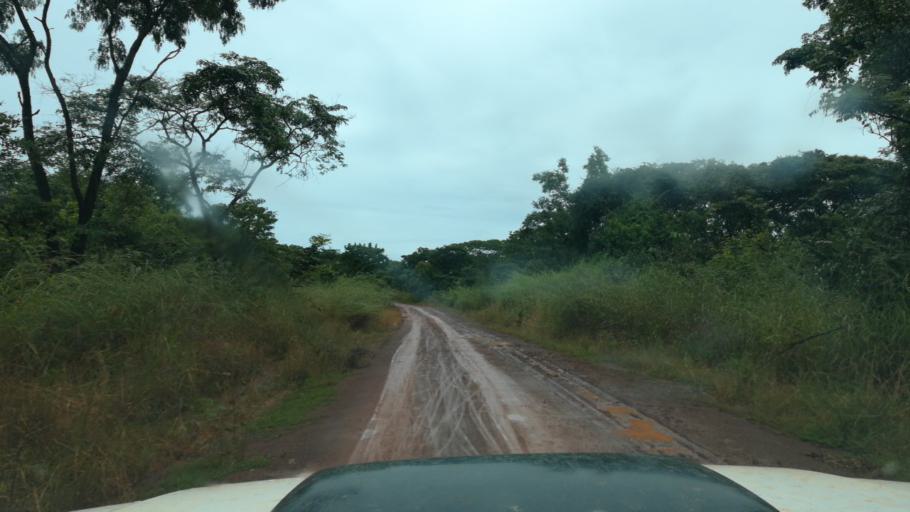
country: ZM
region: Luapula
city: Mwense
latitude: -10.1337
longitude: 28.1227
